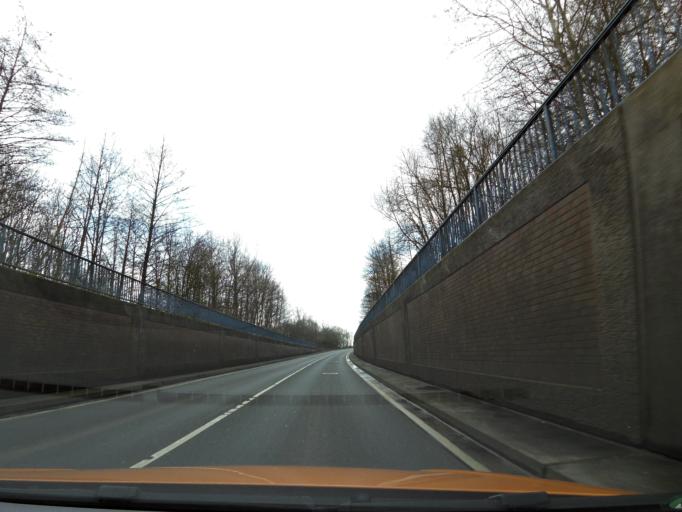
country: DE
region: Lower Saxony
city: Bassum
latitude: 52.8555
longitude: 8.7528
